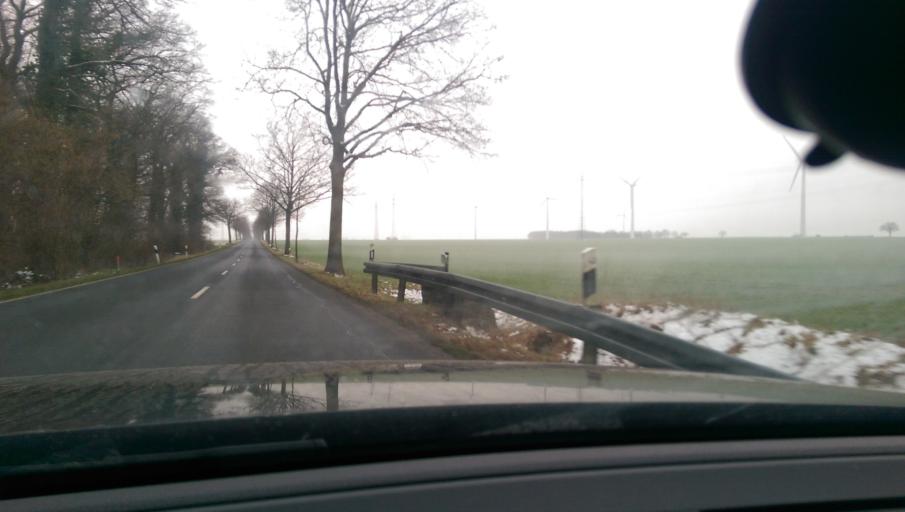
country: DE
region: Lower Saxony
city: Gross Munzel
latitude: 52.3871
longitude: 9.5126
